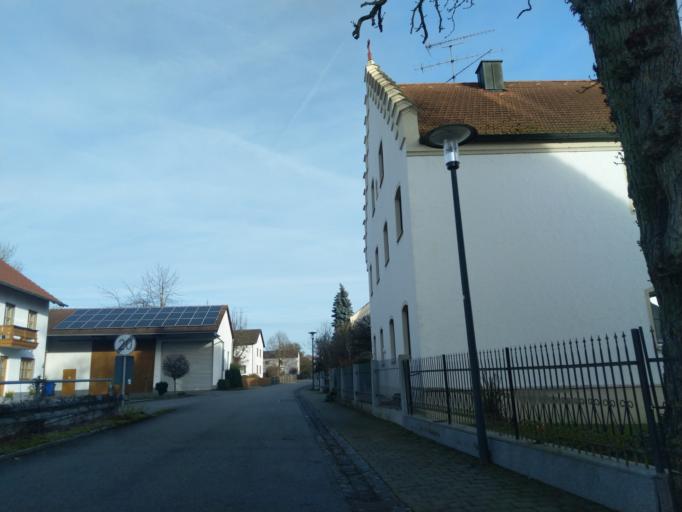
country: DE
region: Bavaria
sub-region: Lower Bavaria
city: Oberporing
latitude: 48.7150
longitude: 12.8461
